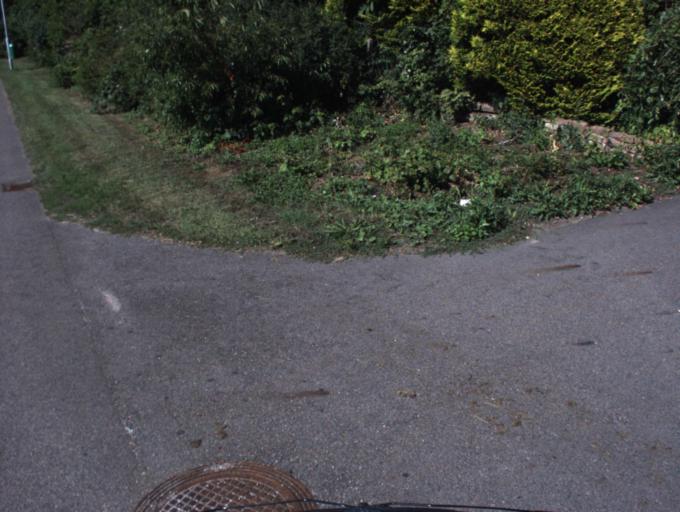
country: SE
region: Skane
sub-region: Helsingborg
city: Helsingborg
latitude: 56.0928
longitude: 12.6525
